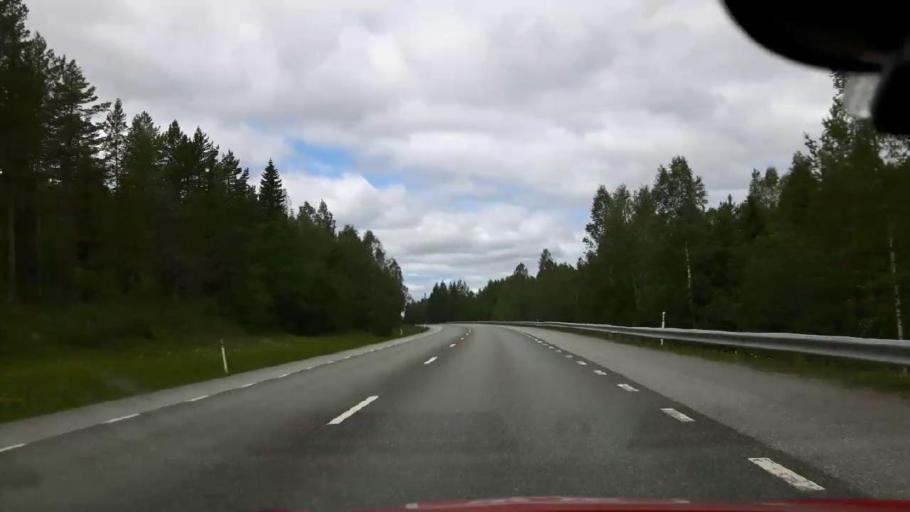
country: SE
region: Jaemtland
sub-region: Braecke Kommun
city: Braecke
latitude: 62.6993
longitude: 15.5205
